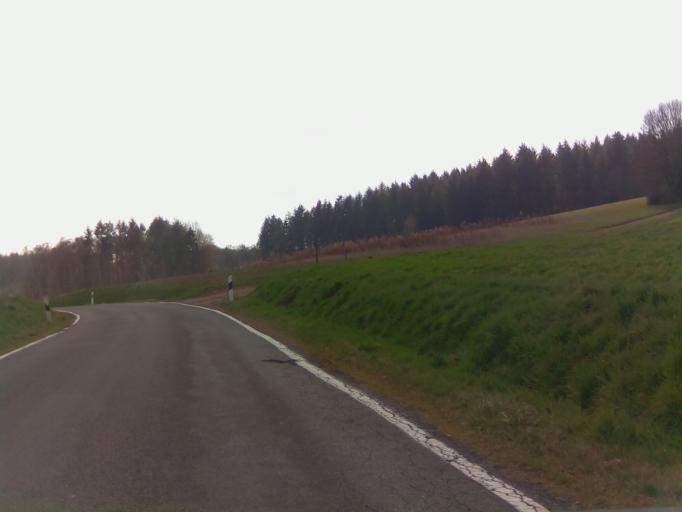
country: DE
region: Rheinland-Pfalz
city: Otzweiler
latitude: 49.7286
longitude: 7.5122
